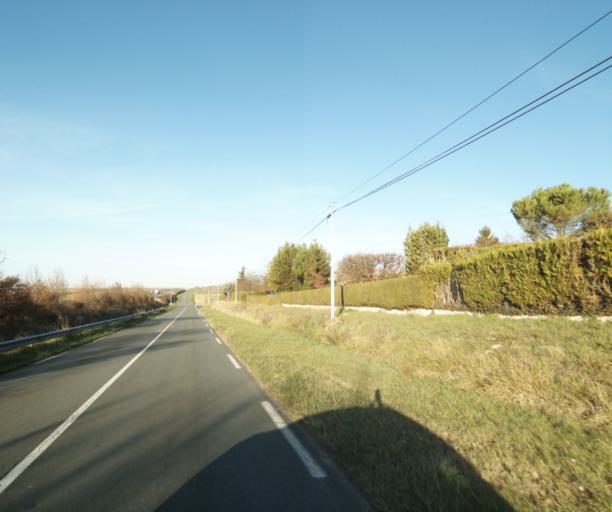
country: FR
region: Poitou-Charentes
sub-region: Departement de la Charente-Maritime
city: Cherac
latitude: 45.7016
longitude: -0.4674
